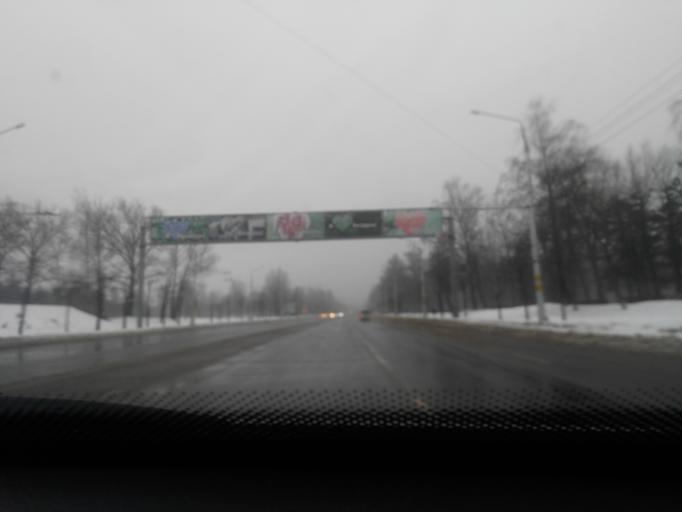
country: BY
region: Mogilev
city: Babruysk
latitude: 53.1769
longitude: 29.1990
